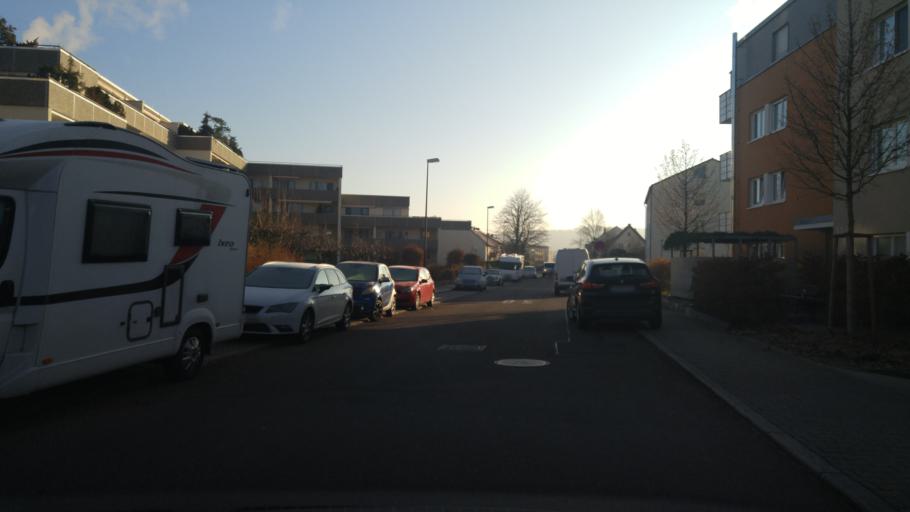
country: DE
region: Baden-Wuerttemberg
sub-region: Regierungsbezirk Stuttgart
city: Gerlingen
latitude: 48.8046
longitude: 9.0598
